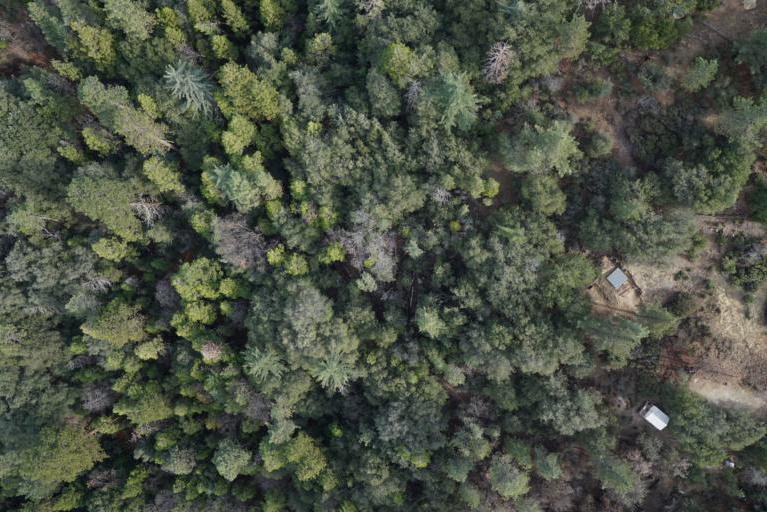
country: US
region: California
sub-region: Riverside County
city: Idyllwild
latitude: 33.7288
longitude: -116.7179
